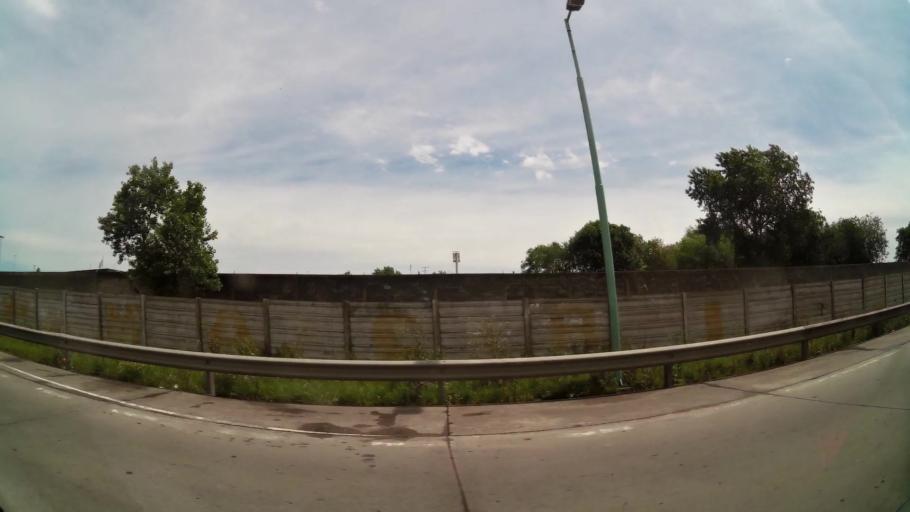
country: AR
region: Buenos Aires F.D.
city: Villa Lugano
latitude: -34.6558
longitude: -58.4615
